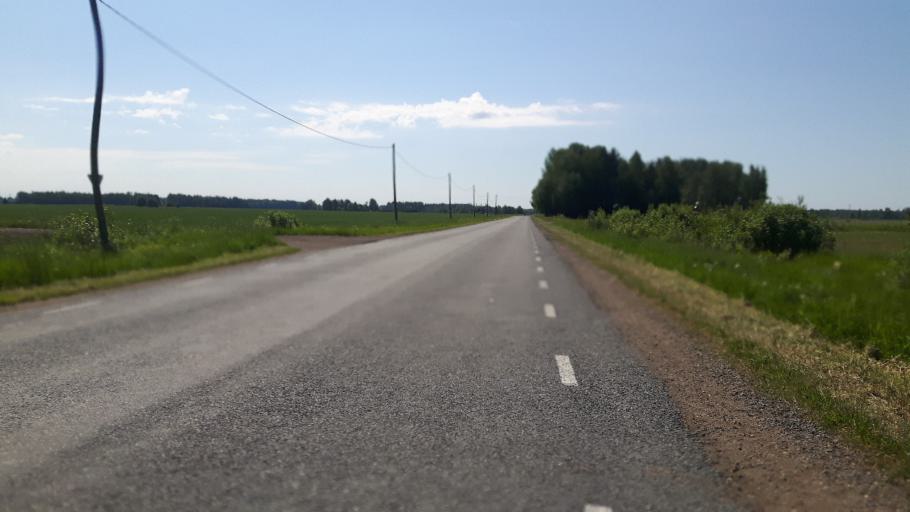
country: EE
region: Paernumaa
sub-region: Vaendra vald (alev)
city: Vandra
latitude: 58.6227
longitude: 25.0210
